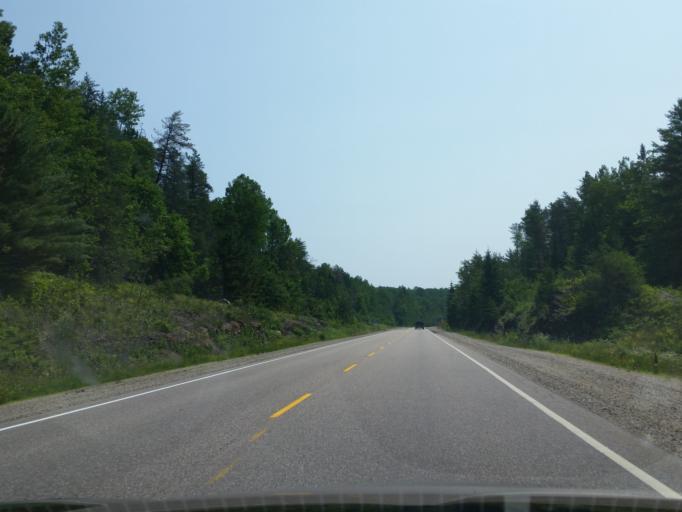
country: CA
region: Ontario
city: Deep River
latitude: 46.1815
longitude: -77.7322
